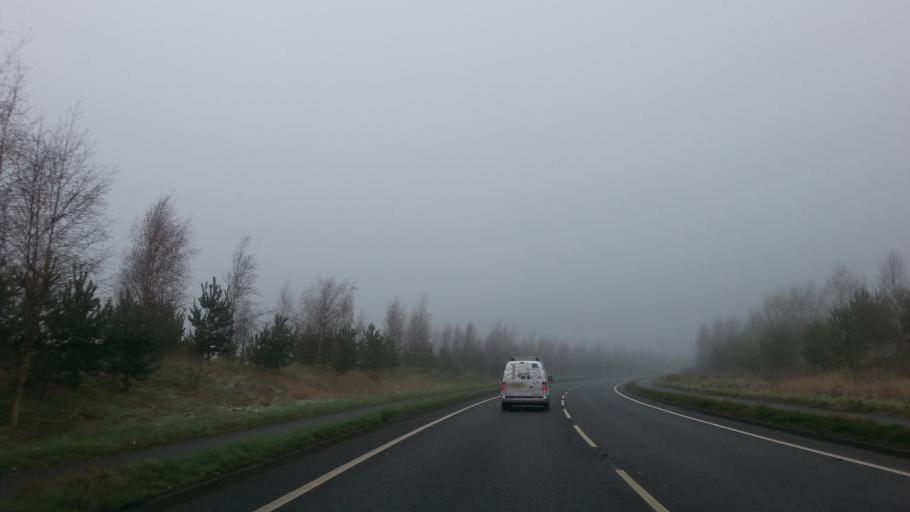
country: GB
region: England
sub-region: Cheshire East
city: Alderley Edge
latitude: 53.2901
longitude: -2.2548
